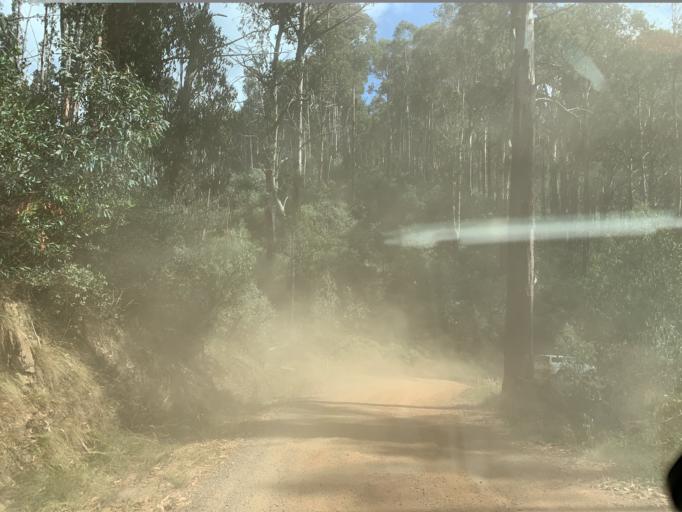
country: AU
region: Victoria
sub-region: Mansfield
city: Mansfield
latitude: -37.0992
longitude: 146.5403
